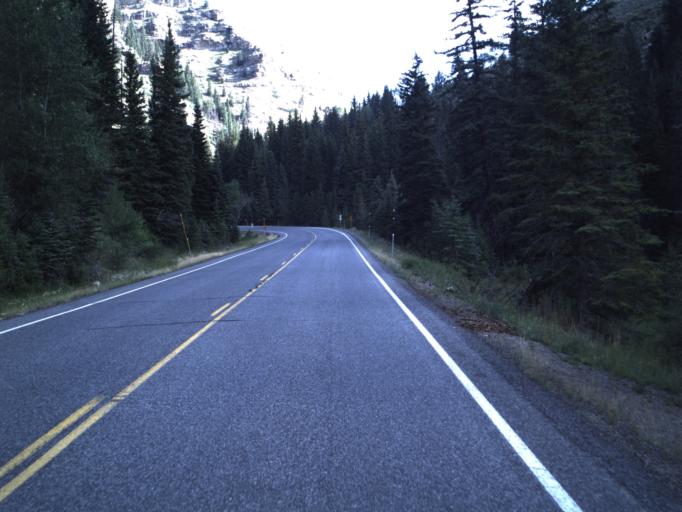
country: US
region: Utah
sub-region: Emery County
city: Huntington
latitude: 39.4975
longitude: -111.1573
